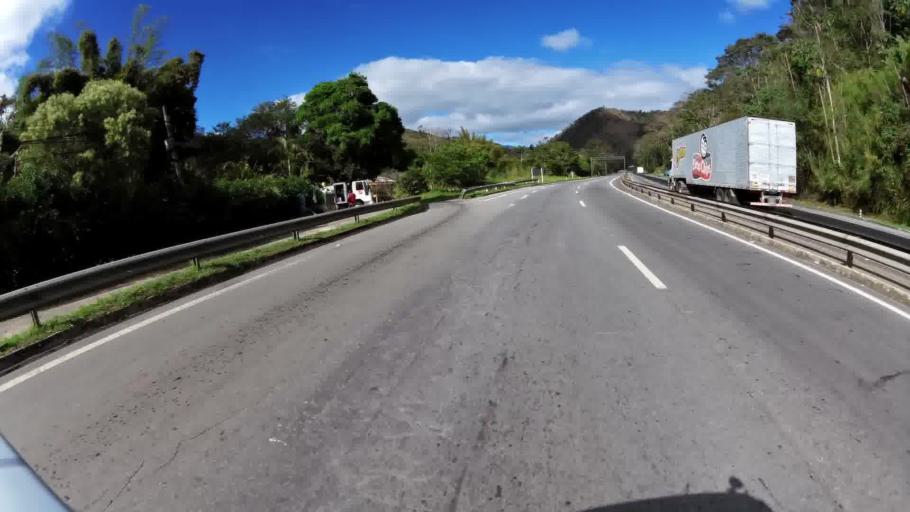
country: BR
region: Rio de Janeiro
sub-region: Areal
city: Areal
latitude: -22.2871
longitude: -43.1218
